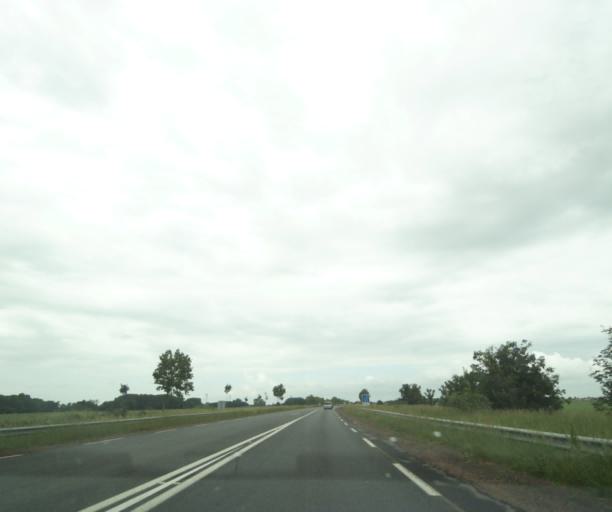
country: FR
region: Poitou-Charentes
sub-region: Departement des Deux-Sevres
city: Saint-Varent
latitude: 46.8365
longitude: -0.2079
